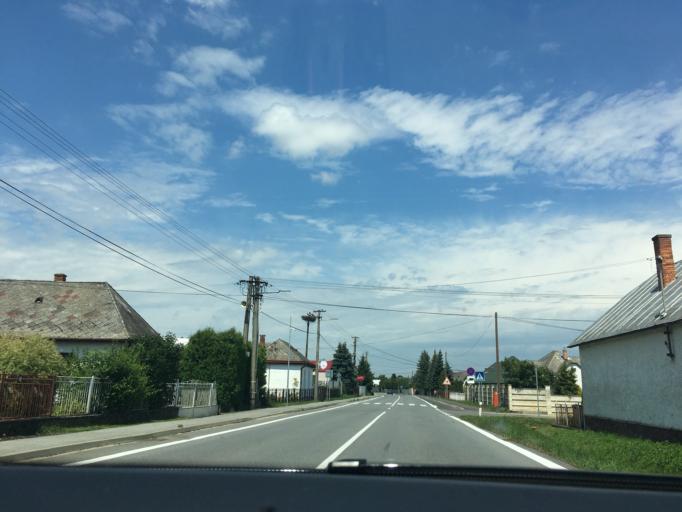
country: SK
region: Presovsky
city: Vranov nad Topl'ou
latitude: 48.8182
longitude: 21.6874
